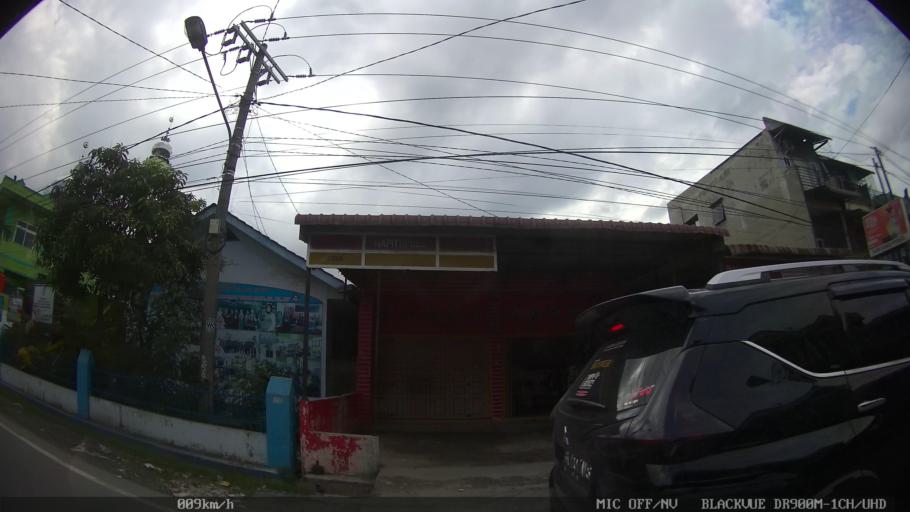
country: ID
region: North Sumatra
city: Sunggal
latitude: 3.6139
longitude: 98.6237
